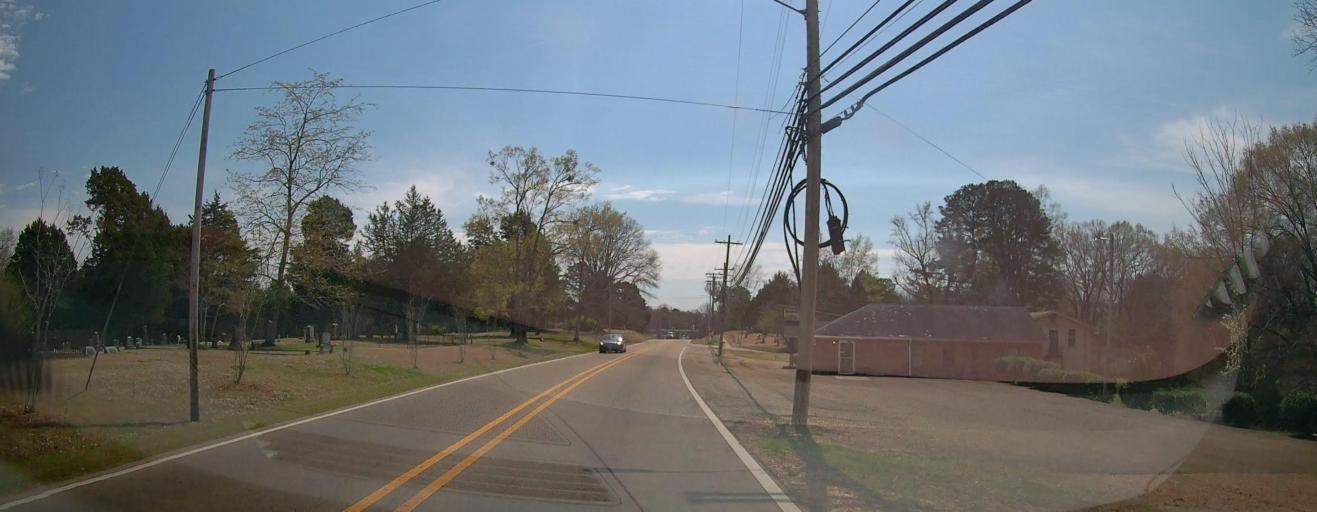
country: US
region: Mississippi
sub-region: Union County
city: New Albany
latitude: 34.4860
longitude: -89.0017
